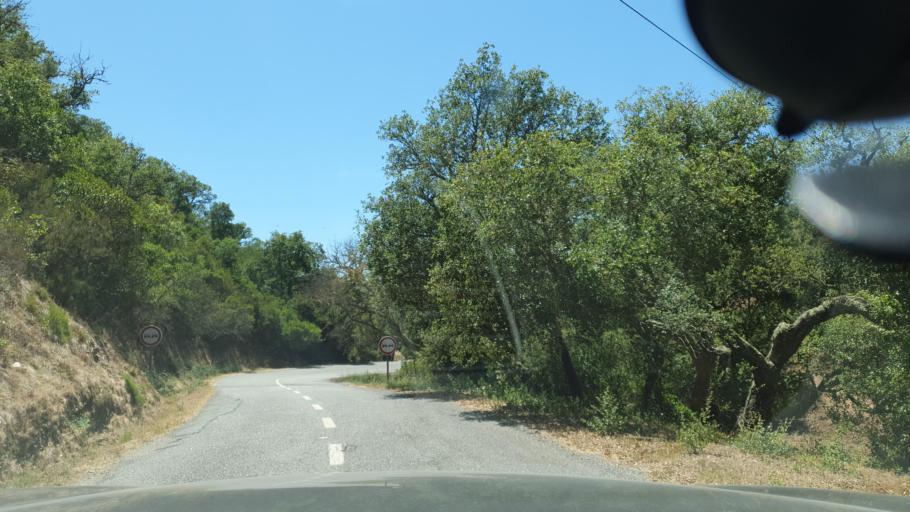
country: PT
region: Beja
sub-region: Odemira
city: Odemira
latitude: 37.6038
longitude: -8.5825
